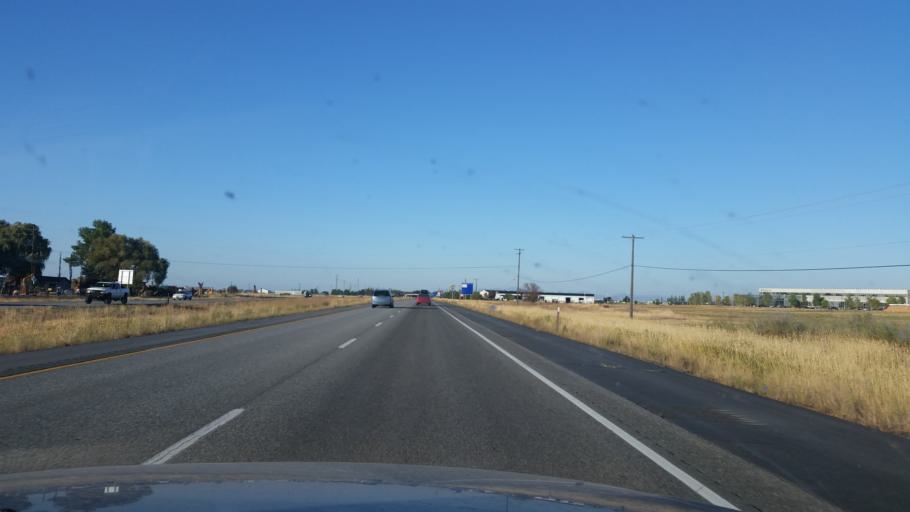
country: US
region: Washington
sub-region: Spokane County
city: Airway Heights
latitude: 47.5809
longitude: -117.5767
